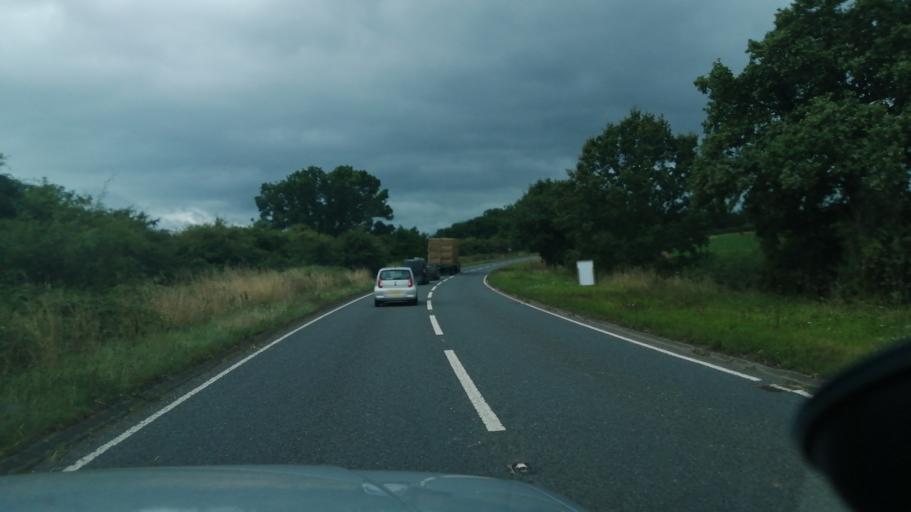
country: GB
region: England
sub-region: Herefordshire
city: Thruxton
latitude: 51.9903
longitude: -2.7907
